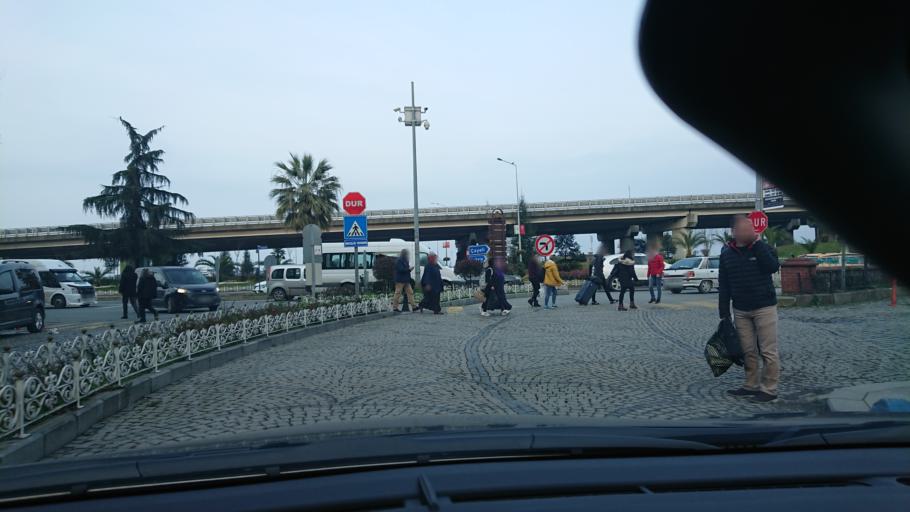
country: TR
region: Rize
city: Rize
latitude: 41.0265
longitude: 40.5182
